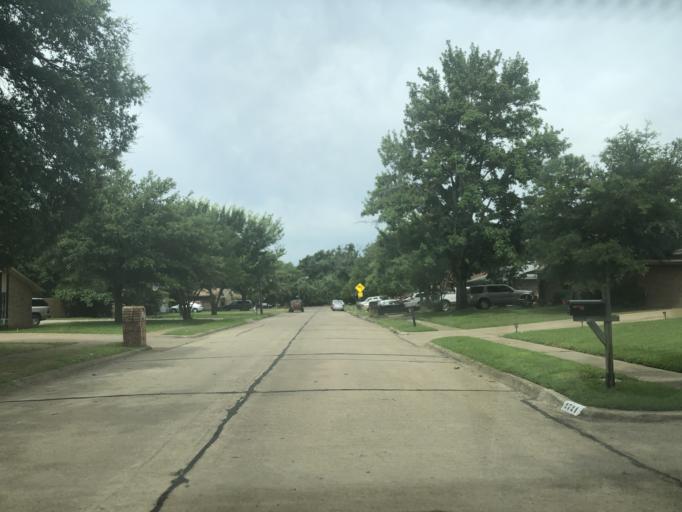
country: US
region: Texas
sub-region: Dallas County
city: Irving
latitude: 32.7935
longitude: -96.9832
